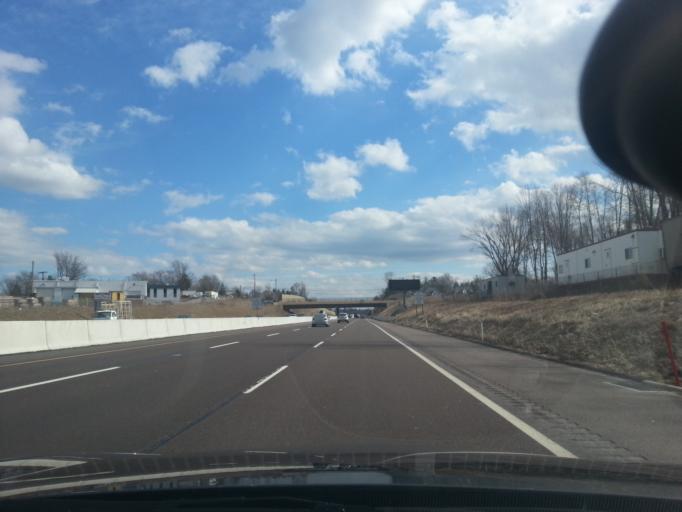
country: US
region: Pennsylvania
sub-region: Montgomery County
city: Blue Bell
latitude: 40.1616
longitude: -75.3001
